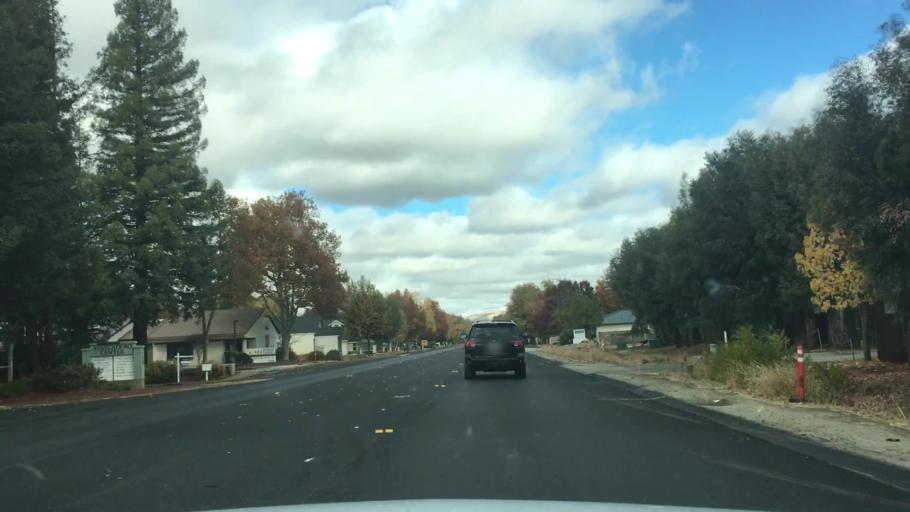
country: US
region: California
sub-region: San Luis Obispo County
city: Atascadero
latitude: 35.4750
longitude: -120.6680
